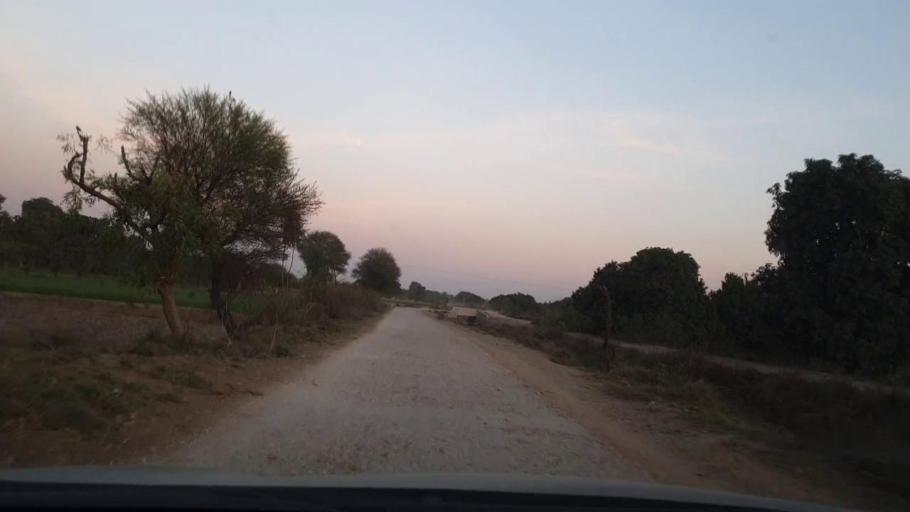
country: PK
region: Sindh
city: Tando Allahyar
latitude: 25.5551
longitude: 68.7875
